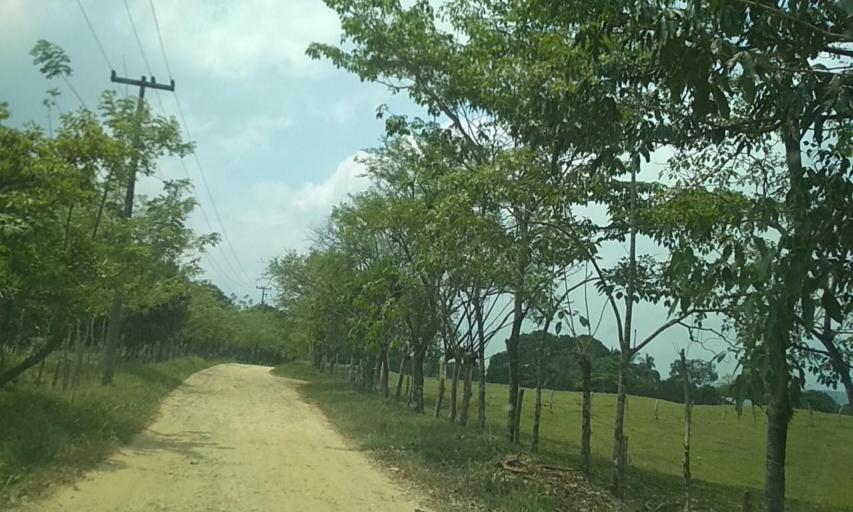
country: MX
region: Tabasco
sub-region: Huimanguillo
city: Francisco Rueda
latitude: 17.5857
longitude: -93.7906
